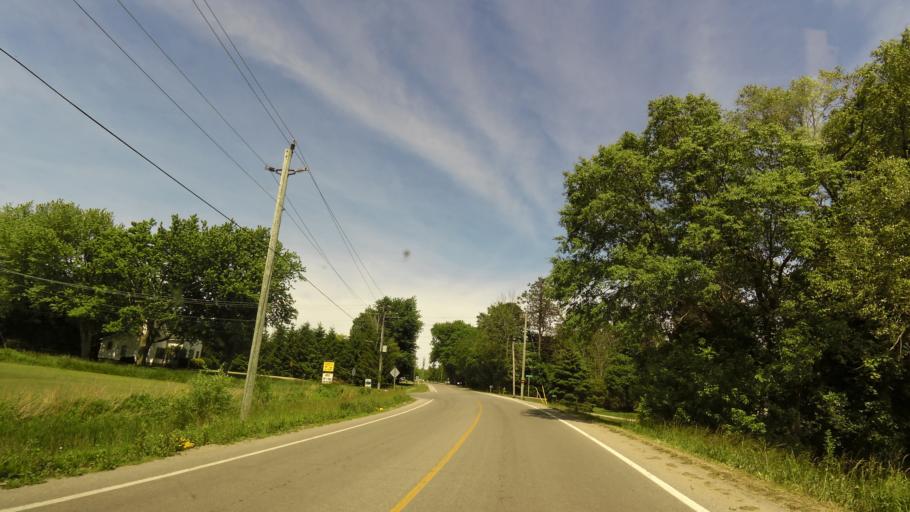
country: CA
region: Ontario
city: Norfolk County
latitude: 42.6645
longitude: -80.4004
